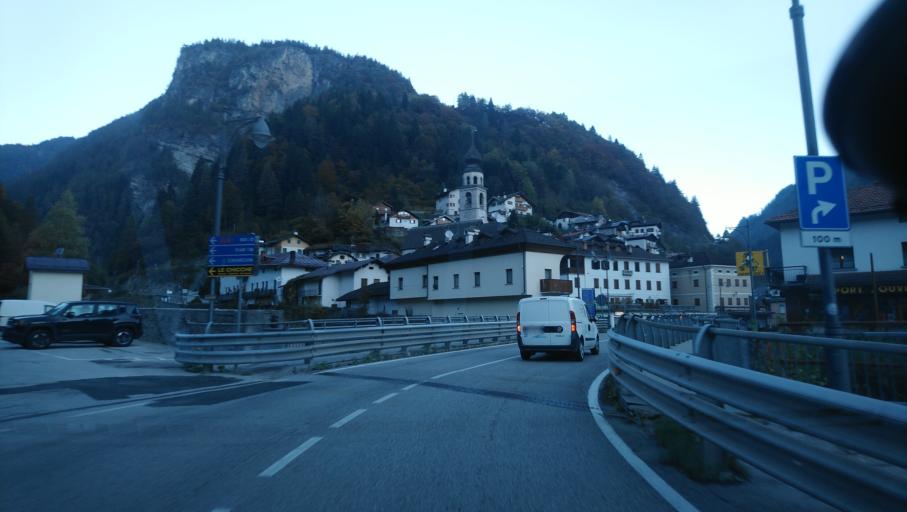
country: IT
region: Veneto
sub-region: Provincia di Belluno
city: Cencenighe Agordino
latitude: 46.3518
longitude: 11.9668
